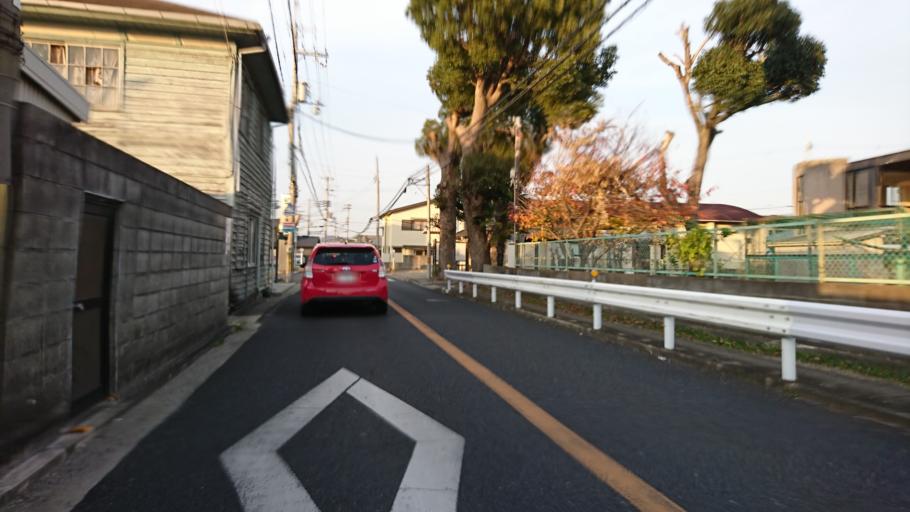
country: JP
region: Hyogo
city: Kakogawacho-honmachi
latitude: 34.7771
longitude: 134.8767
